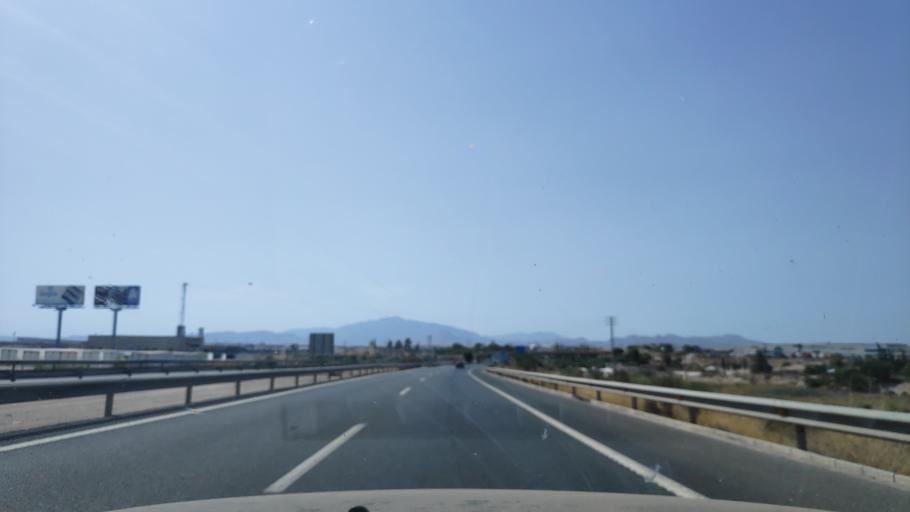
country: ES
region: Murcia
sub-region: Murcia
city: Molina de Segura
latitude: 38.0799
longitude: -1.2148
